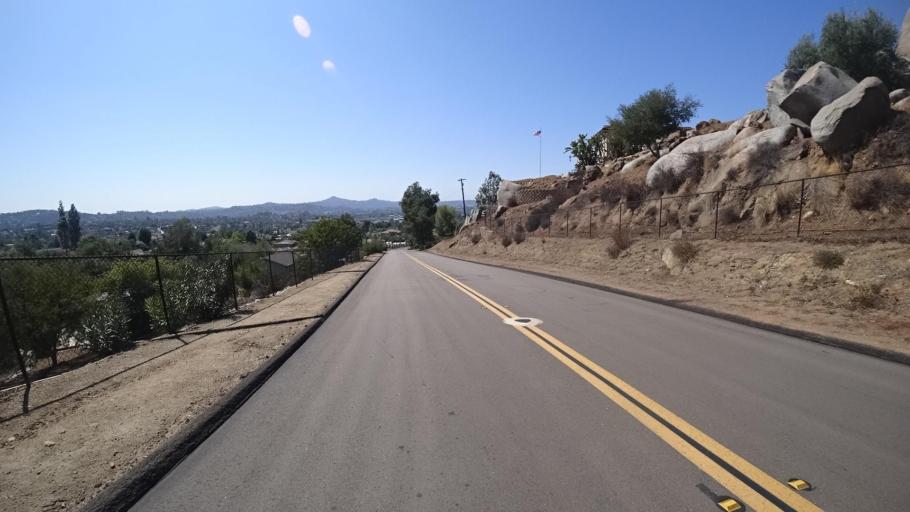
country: US
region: California
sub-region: San Diego County
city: Granite Hills
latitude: 32.8035
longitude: -116.8974
